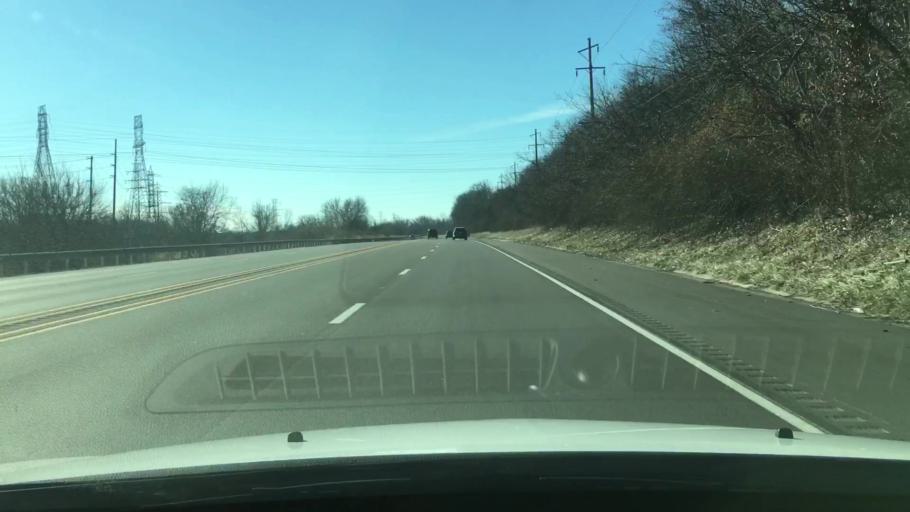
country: US
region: Illinois
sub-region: Tazewell County
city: Pekin
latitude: 40.5985
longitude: -89.6698
